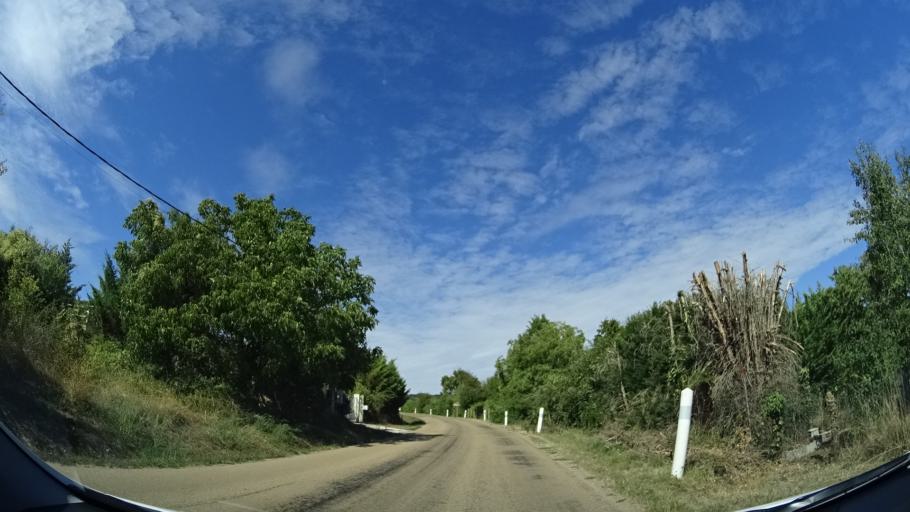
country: FR
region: Bourgogne
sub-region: Departement de l'Yonne
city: Aillant-sur-Tholon
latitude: 47.9191
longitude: 3.3262
